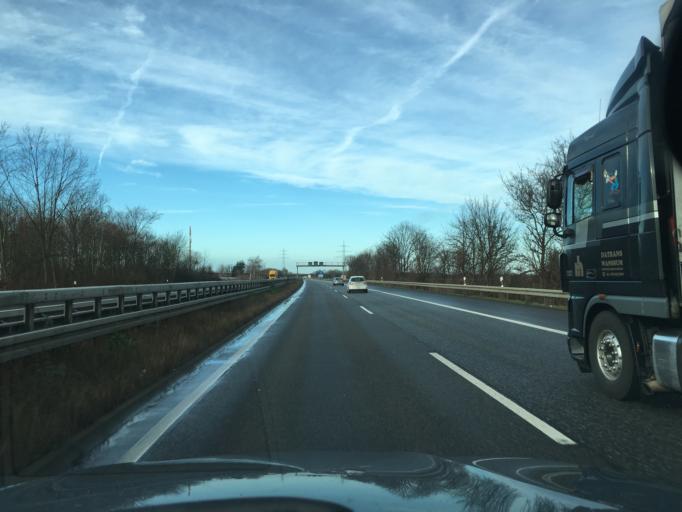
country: DE
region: North Rhine-Westphalia
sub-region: Regierungsbezirk Koln
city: Rheinbach
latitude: 50.6367
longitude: 6.9599
